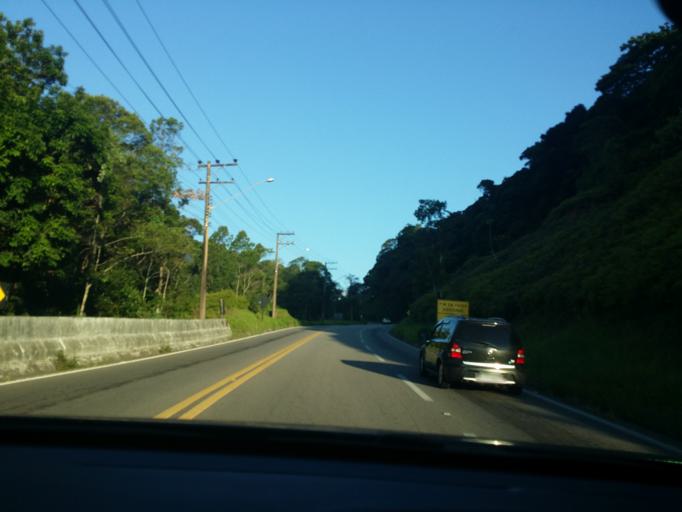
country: BR
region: Sao Paulo
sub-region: Sao Sebastiao
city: Sao Sebastiao
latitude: -23.7820
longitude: -45.5997
